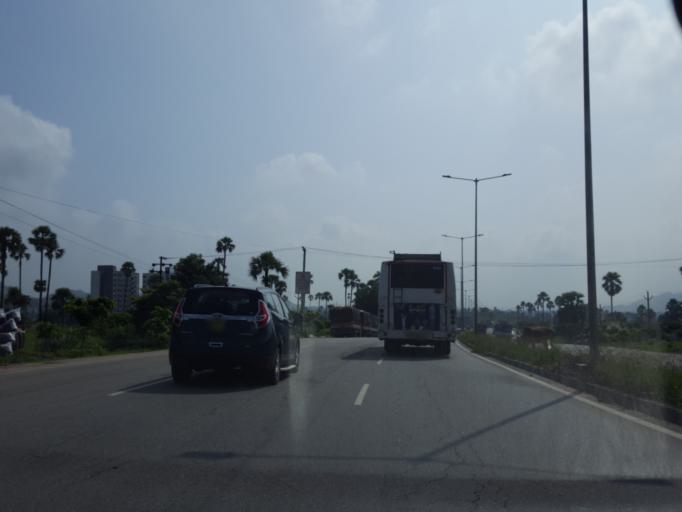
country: IN
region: Telangana
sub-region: Rangareddi
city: Ghatkesar
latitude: 17.3095
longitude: 78.6970
